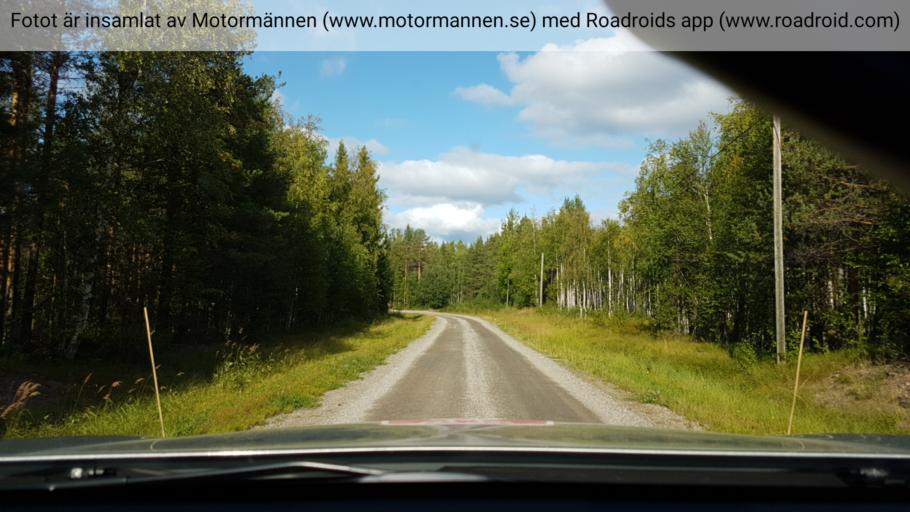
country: SE
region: Vaesterbotten
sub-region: Lycksele Kommun
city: Lycksele
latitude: 64.5634
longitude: 19.0018
